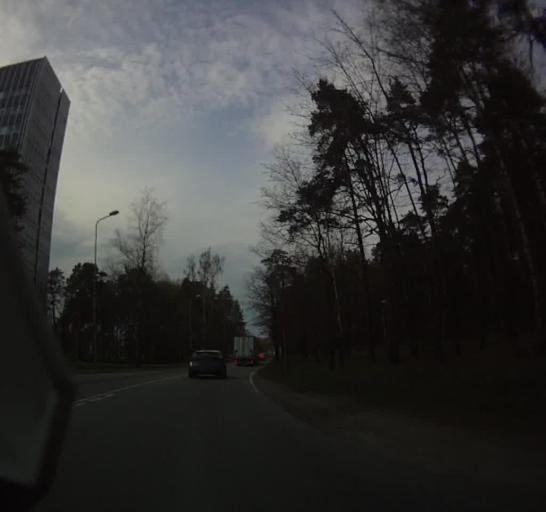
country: LV
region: Riga
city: Jaunciems
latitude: 56.9822
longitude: 24.2102
